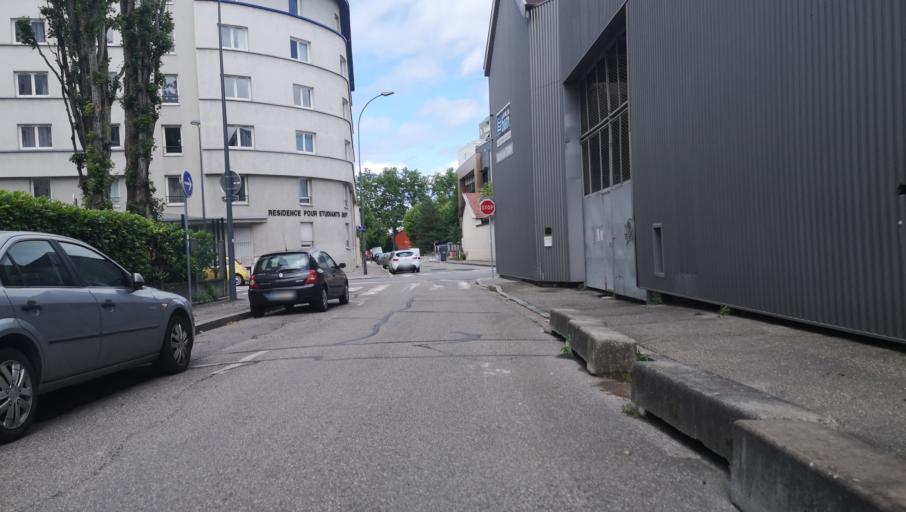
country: FR
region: Rhone-Alpes
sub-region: Departement du Rhone
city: Villeurbanne
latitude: 45.7770
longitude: 4.8696
